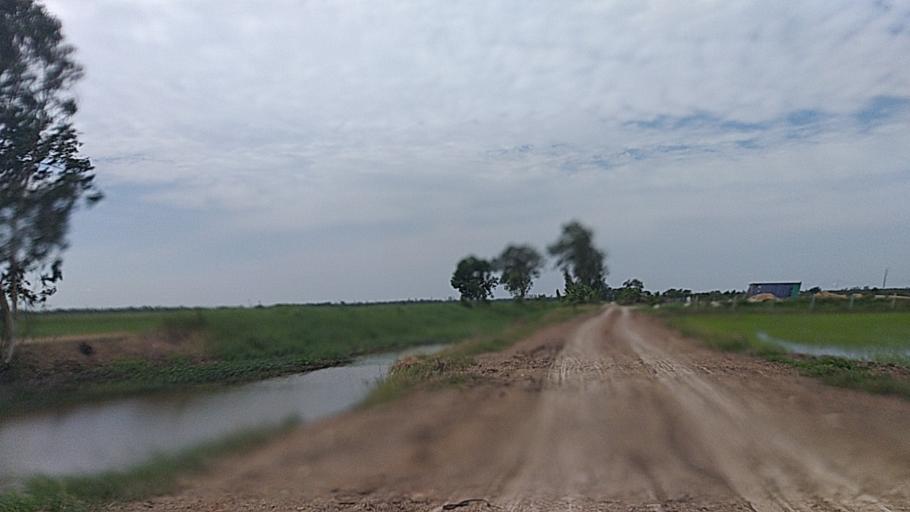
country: TH
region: Pathum Thani
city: Ban Lam Luk Ka
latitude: 14.0256
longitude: 100.8562
